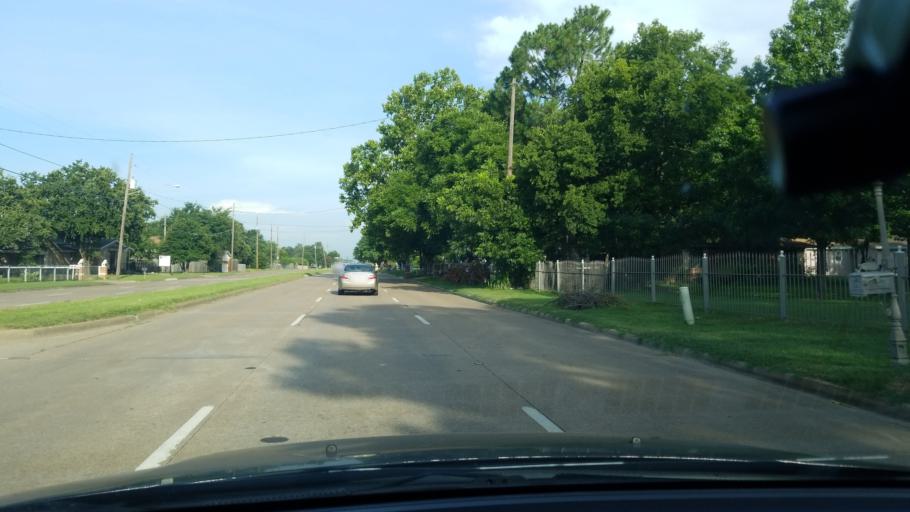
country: US
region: Texas
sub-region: Dallas County
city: Balch Springs
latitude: 32.7487
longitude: -96.6435
